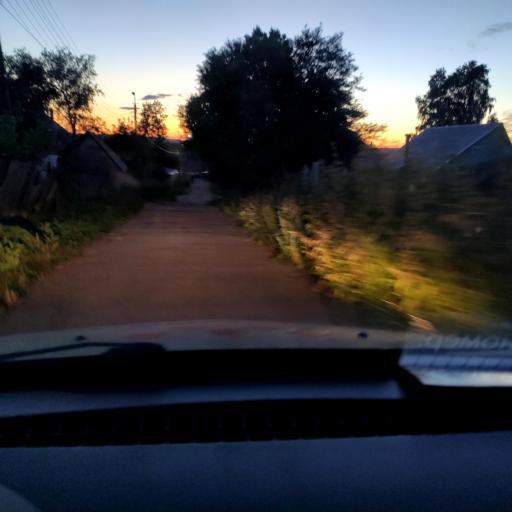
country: RU
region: Bashkortostan
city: Iglino
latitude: 54.7893
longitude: 56.2334
